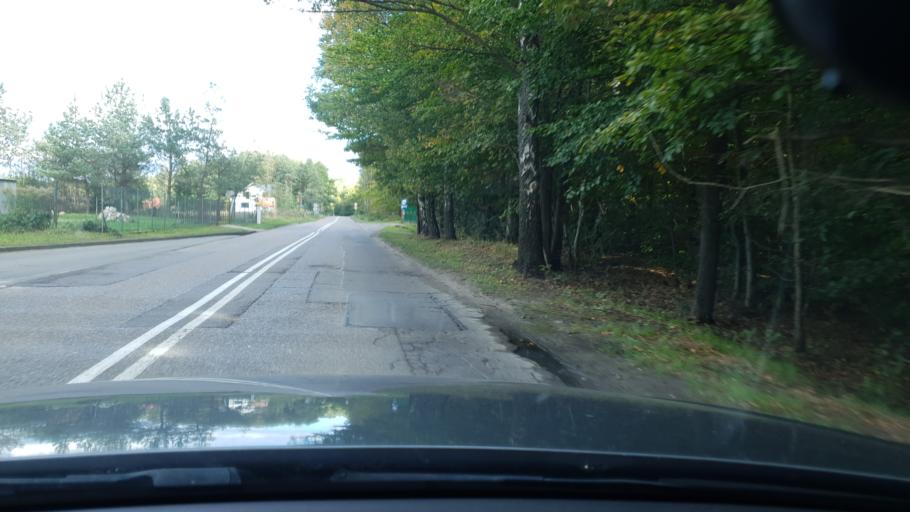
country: PL
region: Pomeranian Voivodeship
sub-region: Powiat wejherowski
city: Bojano
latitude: 54.5062
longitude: 18.3745
